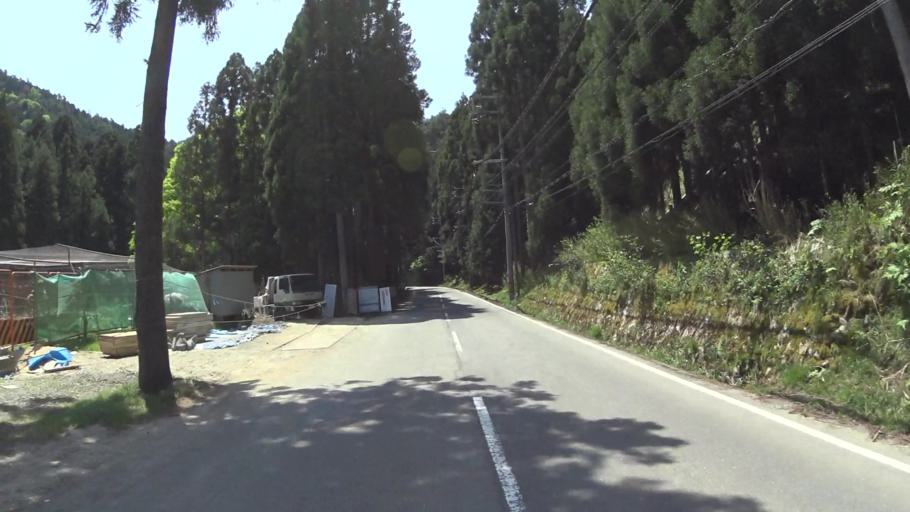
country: JP
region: Kyoto
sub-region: Kyoto-shi
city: Kamigyo-ku
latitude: 35.2024
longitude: 135.7090
